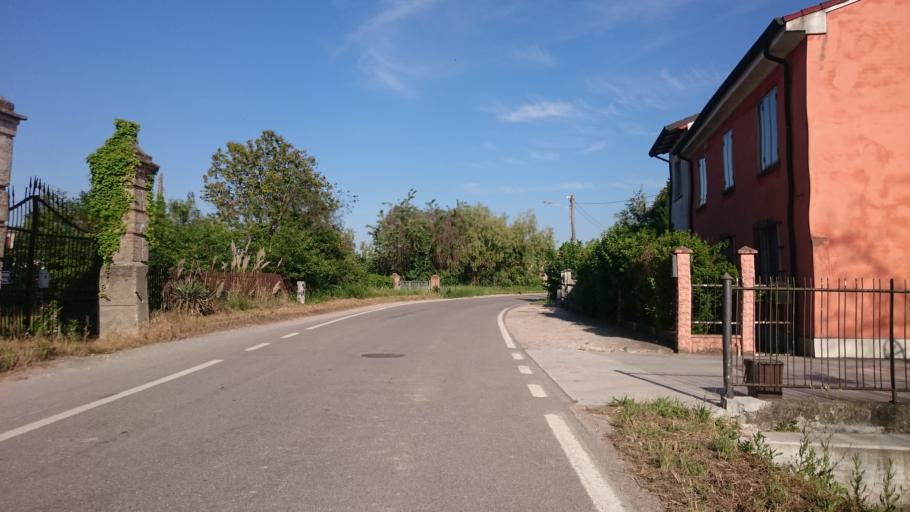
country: IT
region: Lombardy
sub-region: Provincia di Mantova
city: Villimpenta
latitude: 45.1464
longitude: 10.9905
